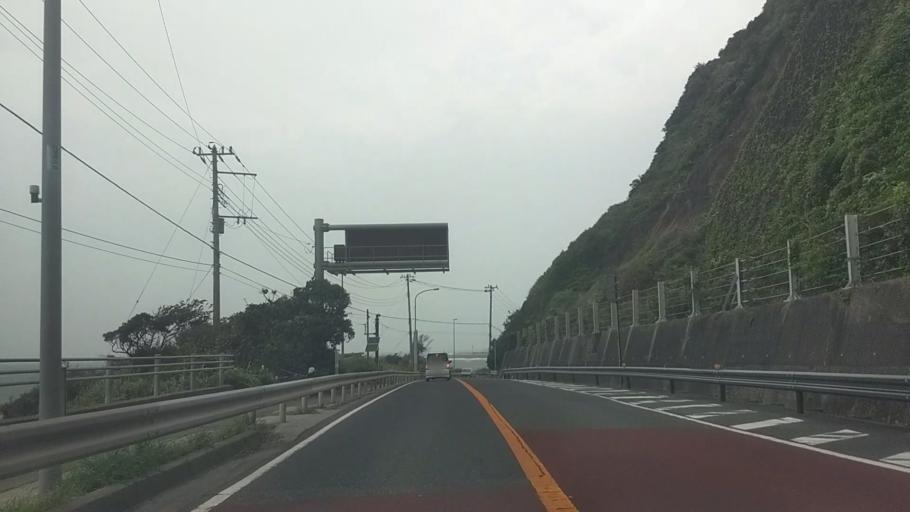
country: JP
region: Chiba
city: Futtsu
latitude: 35.1599
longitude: 139.8199
